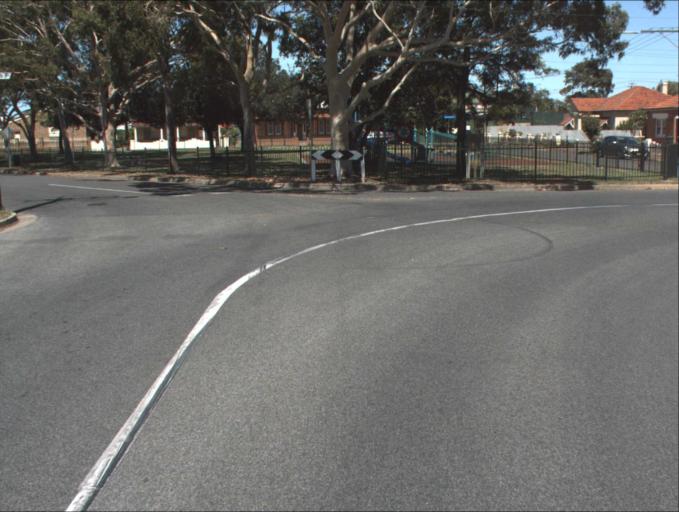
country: AU
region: South Australia
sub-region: Port Adelaide Enfield
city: Cheltenham
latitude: -34.8585
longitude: 138.5052
